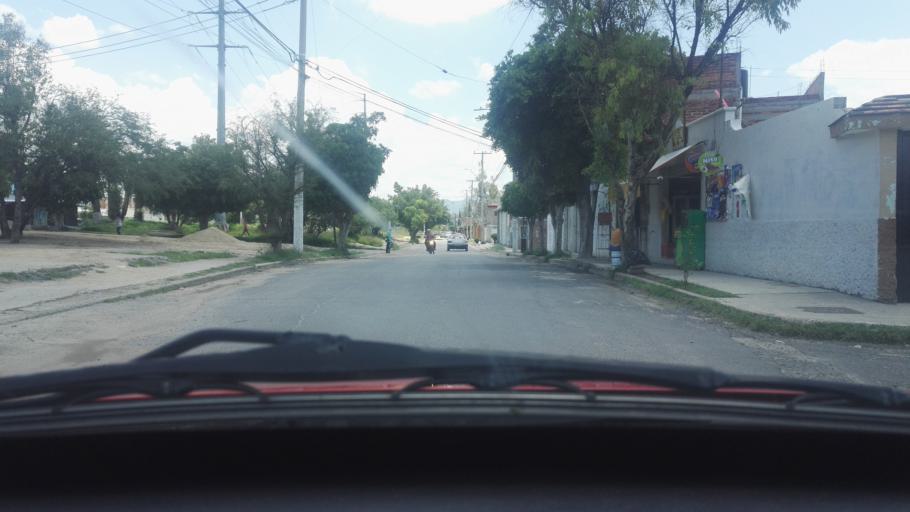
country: MX
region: Guanajuato
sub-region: Leon
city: San Jose de Duran (Los Troncoso)
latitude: 21.0887
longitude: -101.6283
